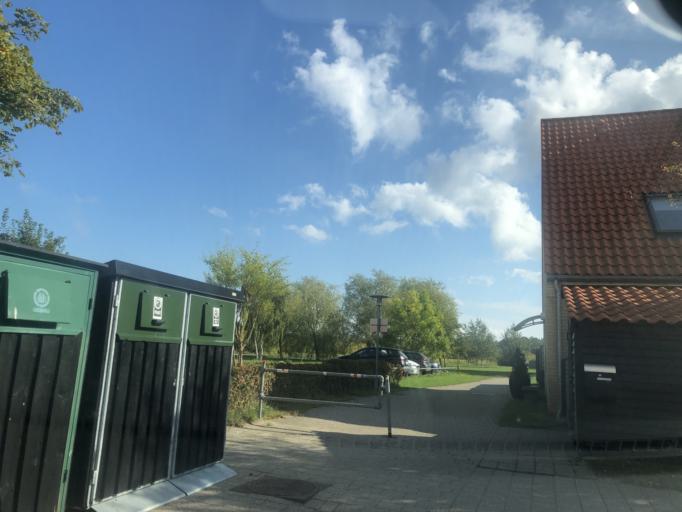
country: DK
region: Capital Region
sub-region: Tarnby Kommune
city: Tarnby
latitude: 55.6084
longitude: 12.5939
